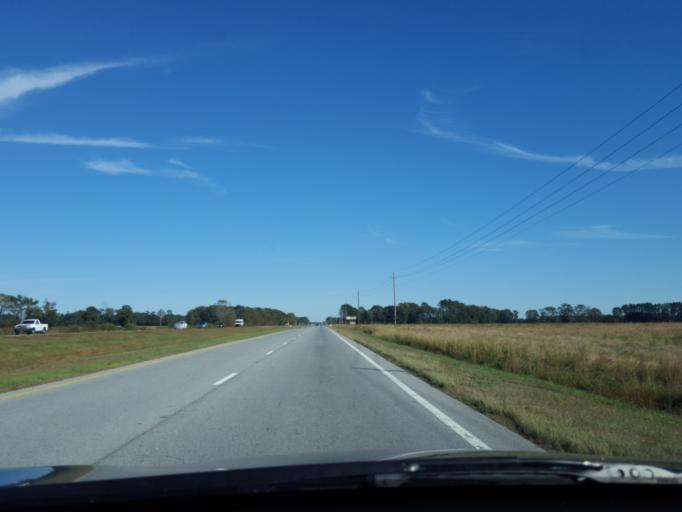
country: US
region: North Carolina
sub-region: Pitt County
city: Greenville
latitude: 35.6257
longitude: -77.3107
